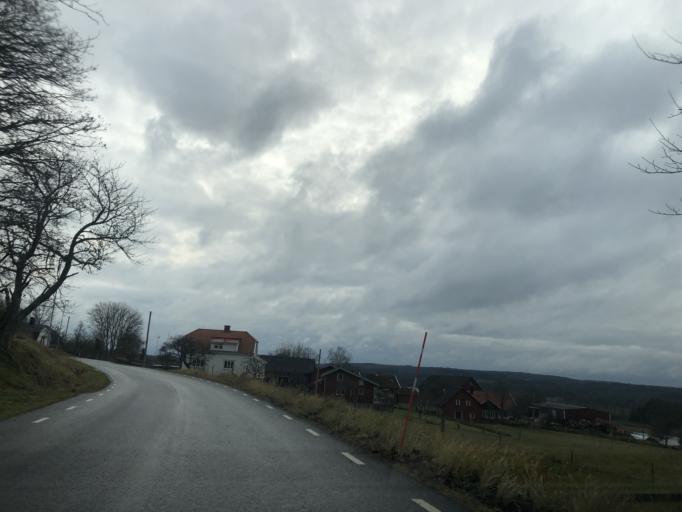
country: SE
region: Vaestra Goetaland
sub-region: Ulricehamns Kommun
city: Ulricehamn
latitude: 57.8258
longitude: 13.2462
